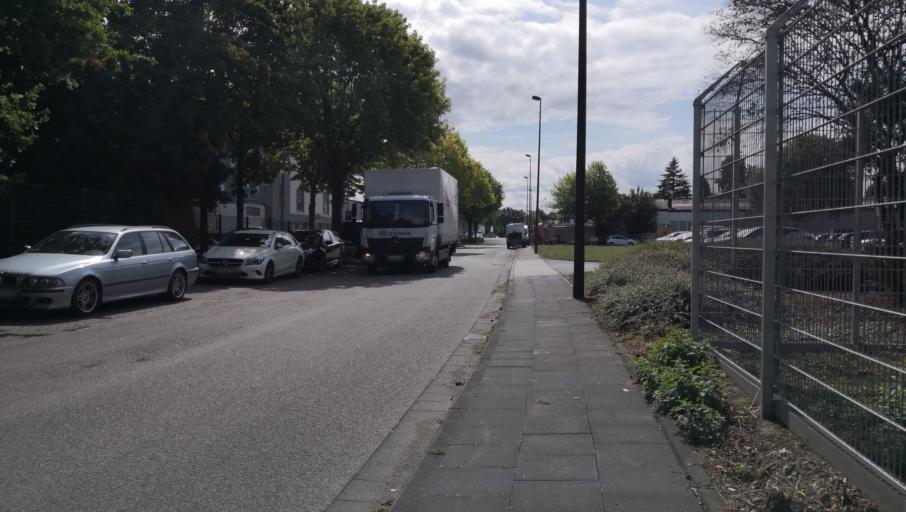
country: DE
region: North Rhine-Westphalia
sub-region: Regierungsbezirk Koln
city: Wahn-Heide
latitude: 50.8395
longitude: 7.1124
